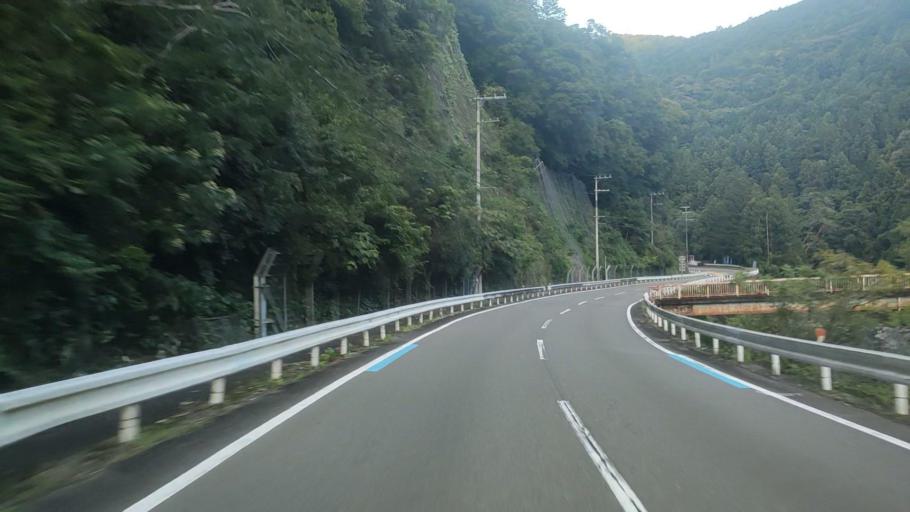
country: JP
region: Wakayama
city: Shingu
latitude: 33.8064
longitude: 135.7323
